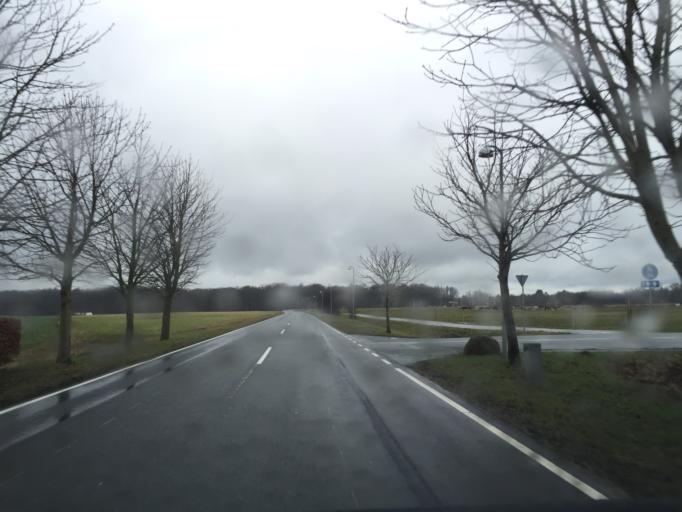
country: DK
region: Capital Region
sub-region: Fureso Kommune
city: Farum
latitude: 55.8164
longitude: 12.3423
